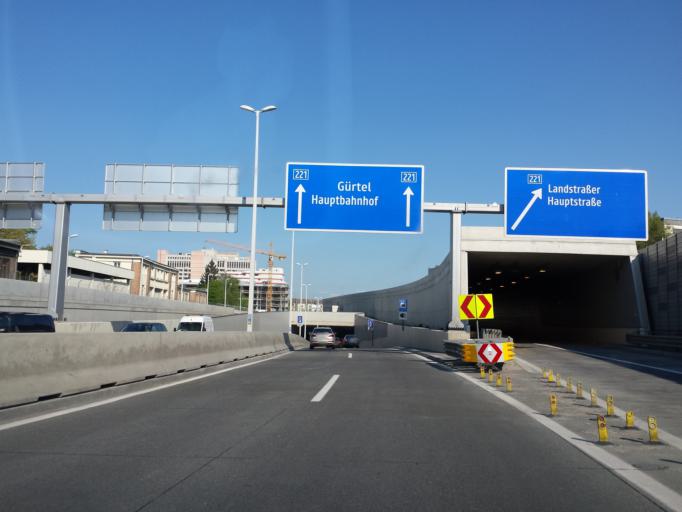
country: AT
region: Vienna
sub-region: Wien Stadt
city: Vienna
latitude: 48.1838
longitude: 16.3984
